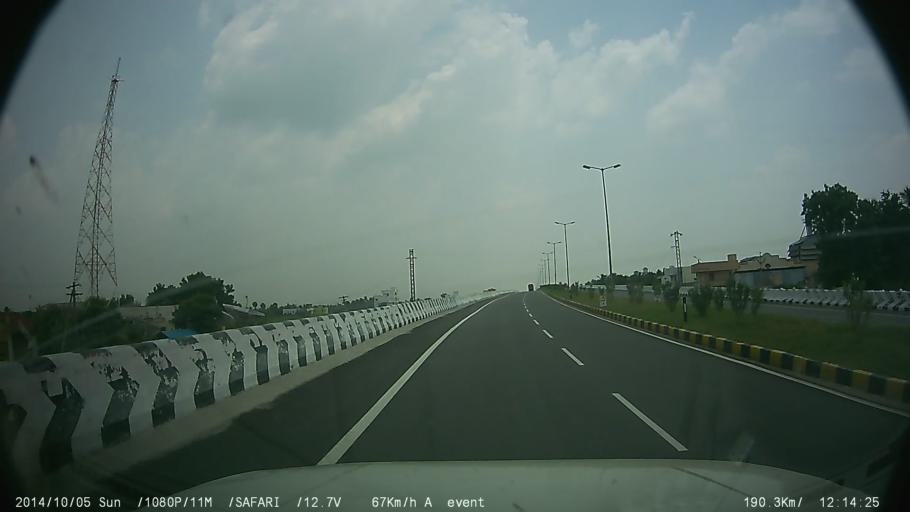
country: IN
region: Tamil Nadu
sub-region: Villupuram
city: Kallakkurichchi
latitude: 11.7376
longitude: 78.9907
